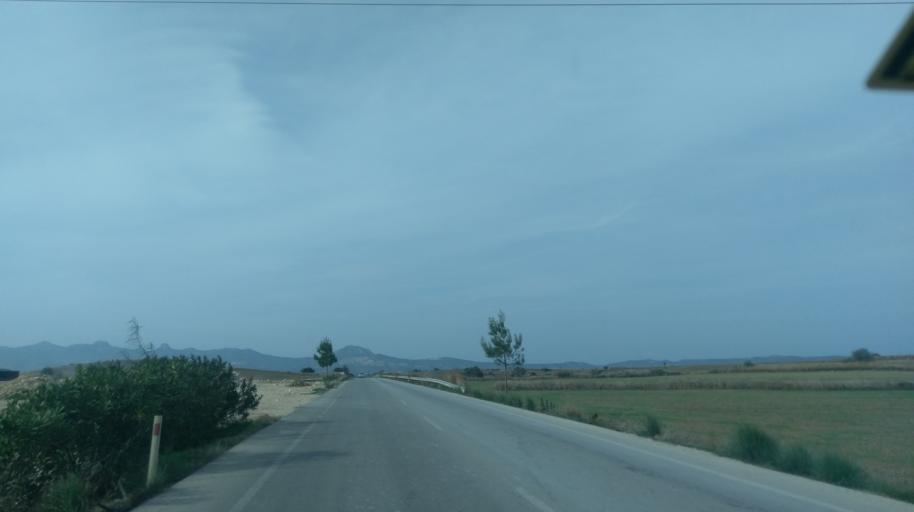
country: CY
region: Ammochostos
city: Leonarisso
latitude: 35.3741
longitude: 34.0307
